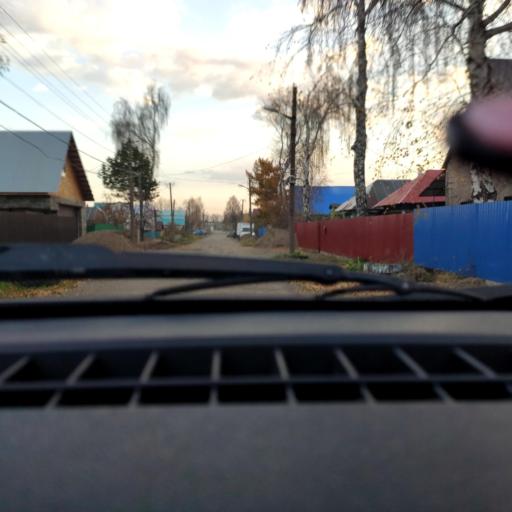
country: RU
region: Bashkortostan
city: Iglino
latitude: 54.8313
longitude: 56.1846
